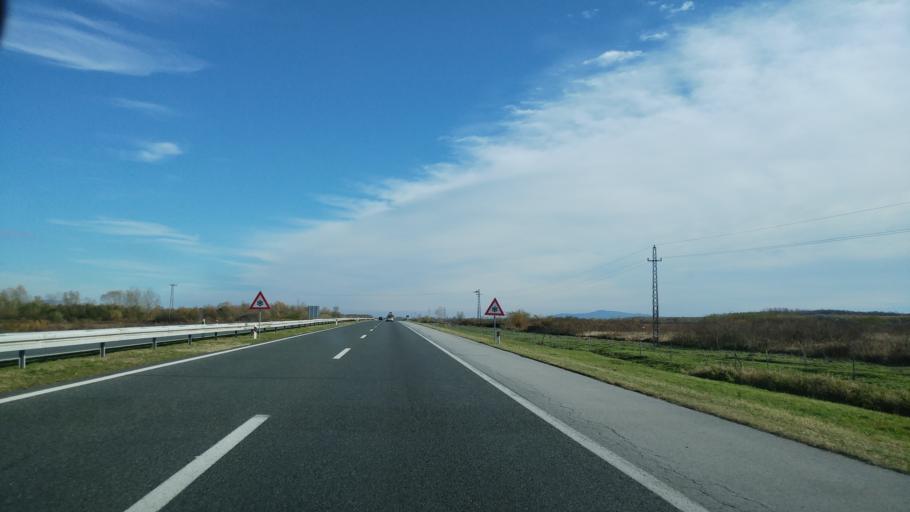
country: HR
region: Brodsko-Posavska
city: Ljupina
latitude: 45.2311
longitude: 17.3083
